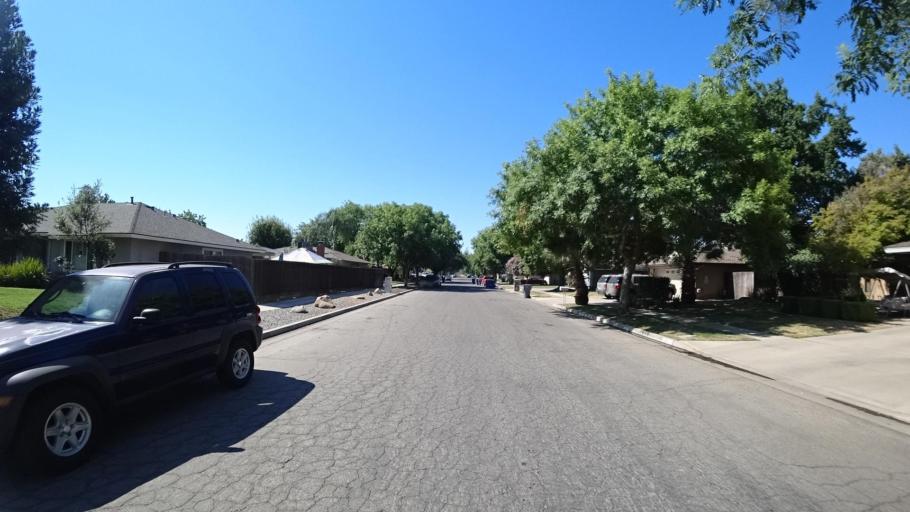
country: US
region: California
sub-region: Fresno County
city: Sunnyside
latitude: 36.7480
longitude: -119.6866
